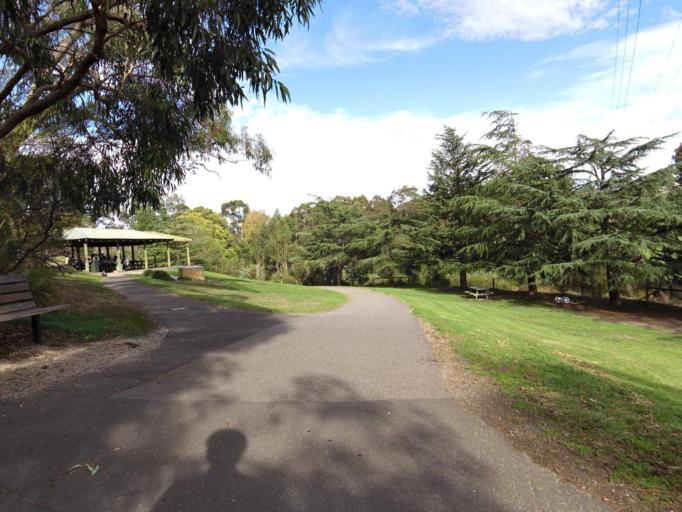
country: AU
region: Victoria
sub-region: Manningham
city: Doncaster East
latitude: -37.7774
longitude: 145.1438
